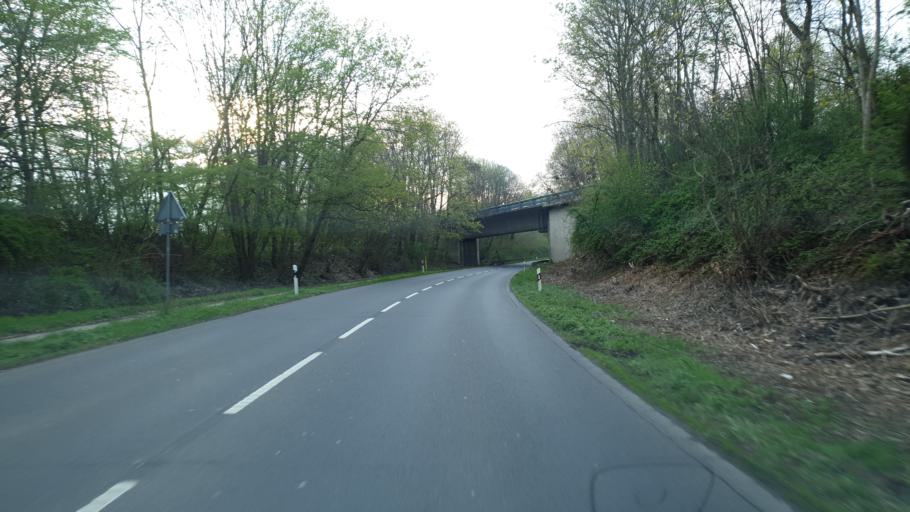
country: DE
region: North Rhine-Westphalia
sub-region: Regierungsbezirk Koln
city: Frechen
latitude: 50.9059
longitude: 6.7682
